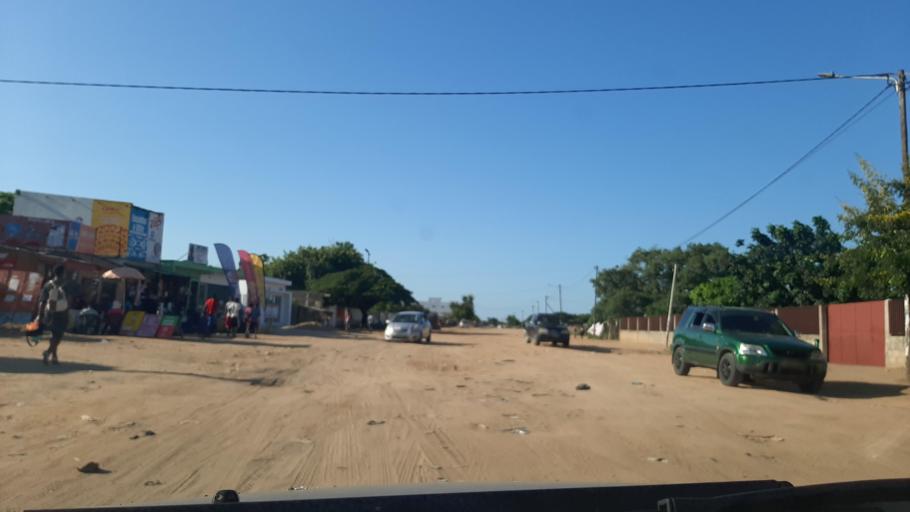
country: MZ
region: Maputo City
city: Maputo
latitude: -25.8086
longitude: 32.5462
